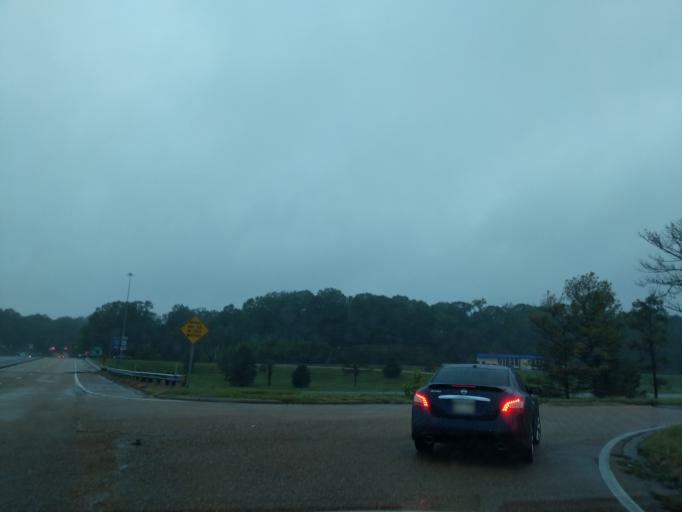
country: US
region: Mississippi
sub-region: Warren County
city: Vicksburg
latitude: 32.3299
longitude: -90.8599
